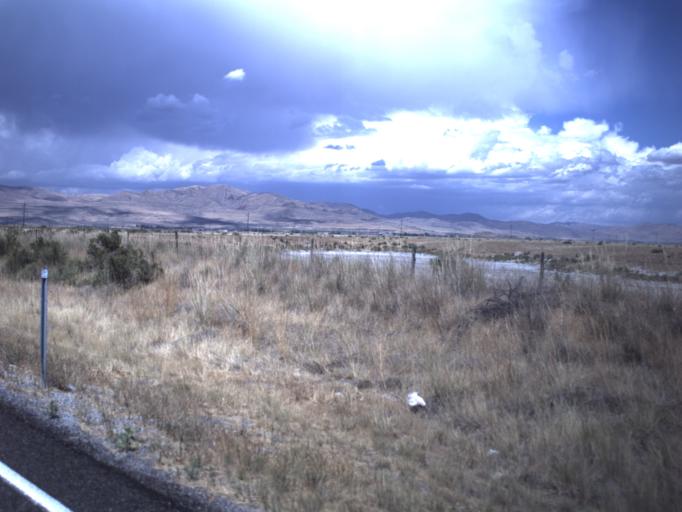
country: US
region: Utah
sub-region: Box Elder County
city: Tremonton
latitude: 41.5890
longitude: -112.2709
